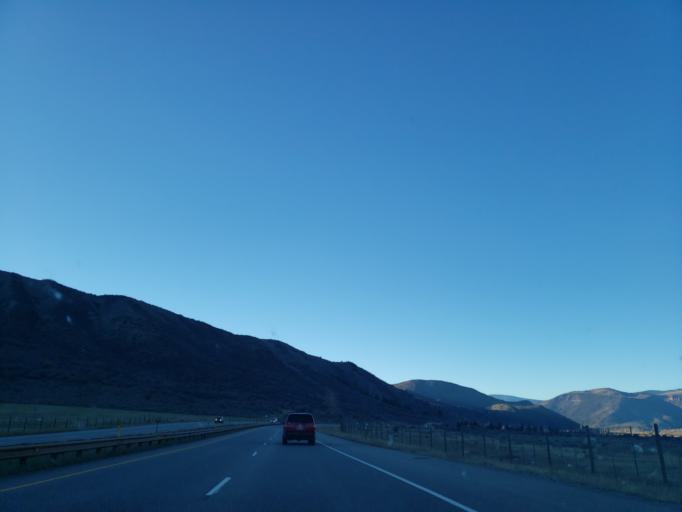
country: US
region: Colorado
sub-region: Pitkin County
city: Snowmass Village
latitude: 39.2354
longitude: -106.8732
